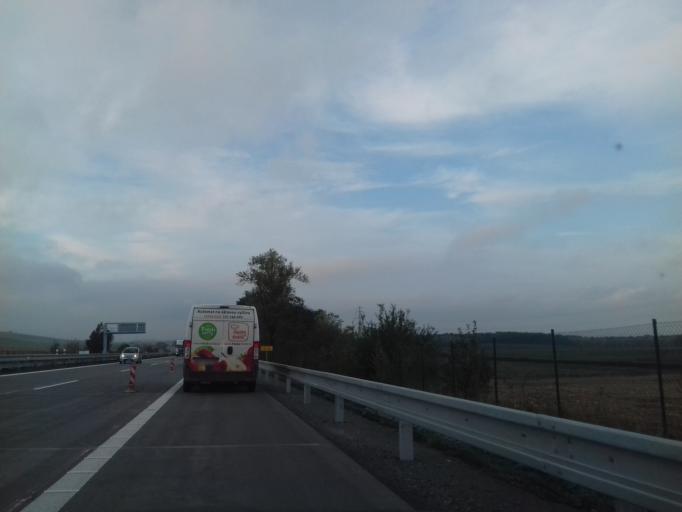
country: CZ
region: South Moravian
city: Velke Nemcice
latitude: 49.0208
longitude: 16.6861
